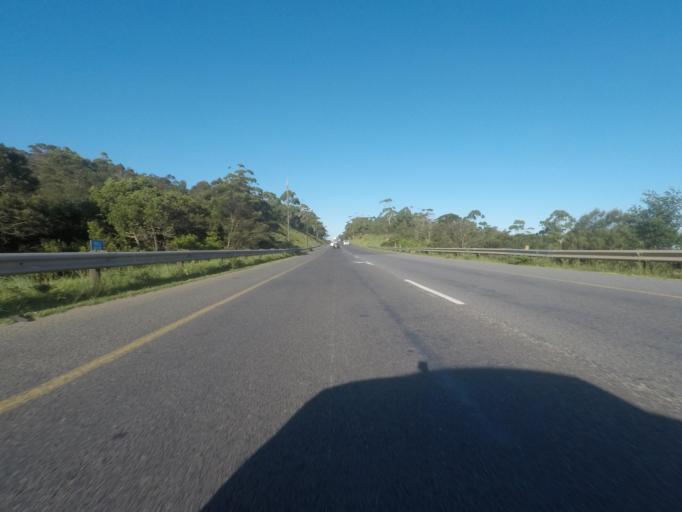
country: ZA
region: Eastern Cape
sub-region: Buffalo City Metropolitan Municipality
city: East London
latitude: -33.0474
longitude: 27.8212
